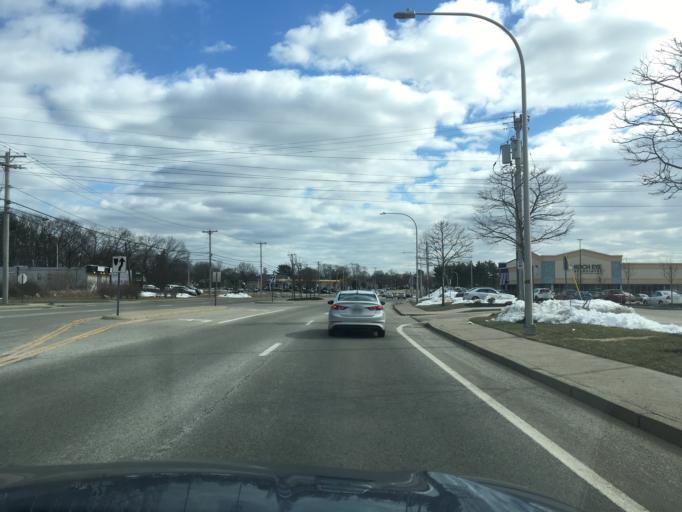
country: US
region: Rhode Island
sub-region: Kent County
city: Warwick
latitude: 41.7192
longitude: -71.4644
